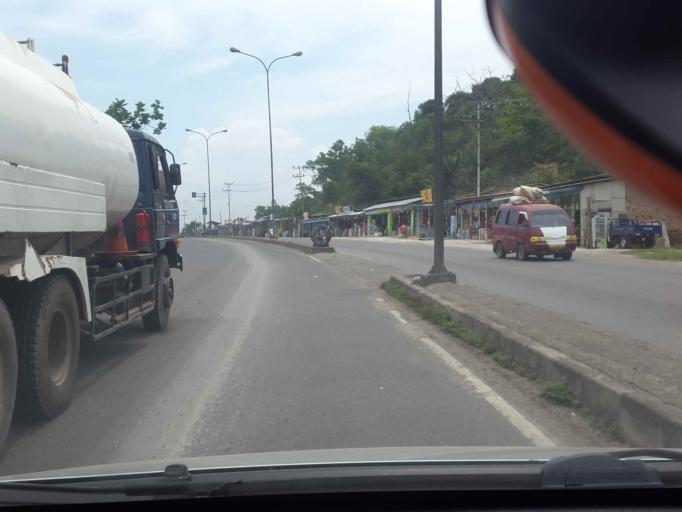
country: ID
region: Lampung
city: Panjang
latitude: -5.4615
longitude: 105.3206
